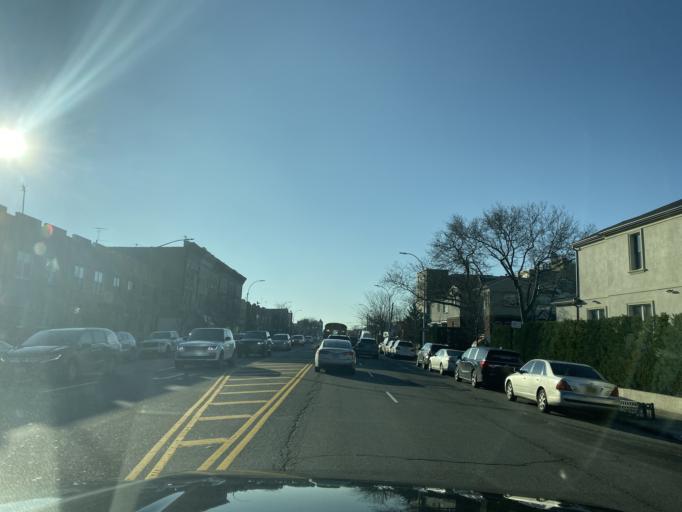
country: US
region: New York
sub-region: Kings County
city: Bensonhurst
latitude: 40.6051
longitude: -73.9618
